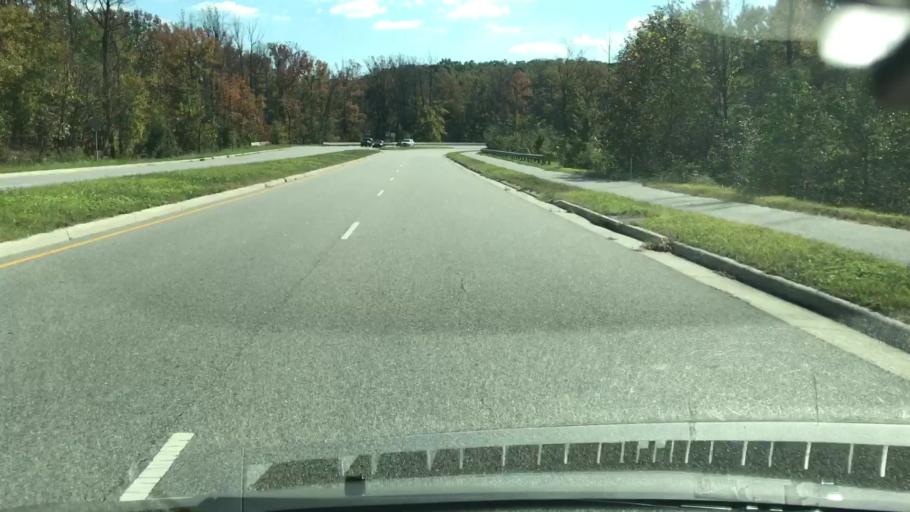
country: US
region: Virginia
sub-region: Fairfax County
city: Hayfield
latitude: 38.7424
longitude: -77.1485
